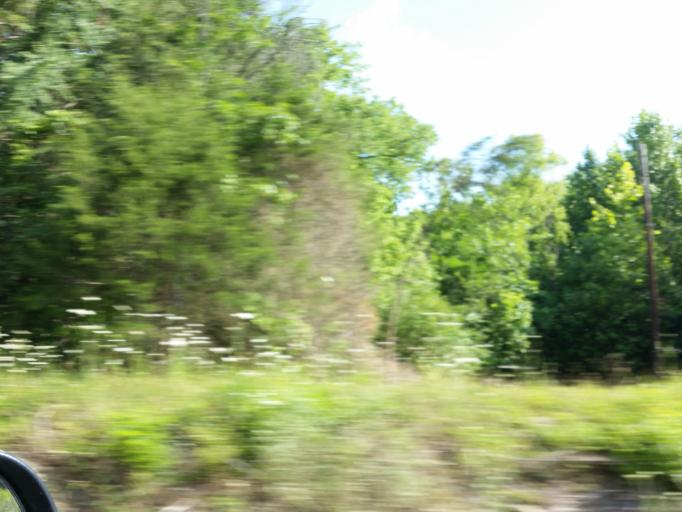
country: US
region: Tennessee
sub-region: Perry County
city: Linden
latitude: 35.6331
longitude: -87.7734
